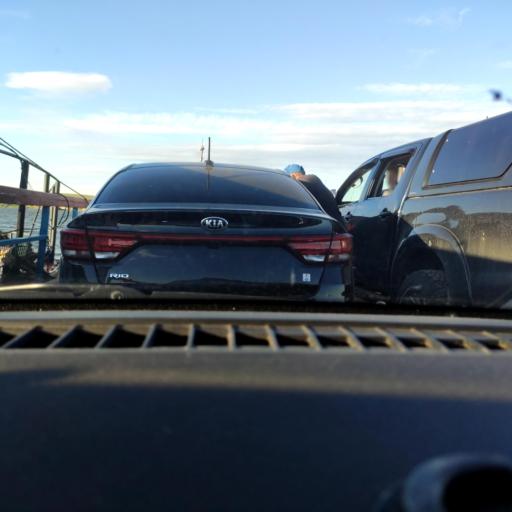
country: RU
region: Perm
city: Verkhnechusovskiye Gorodki
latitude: 58.1880
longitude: 57.1223
